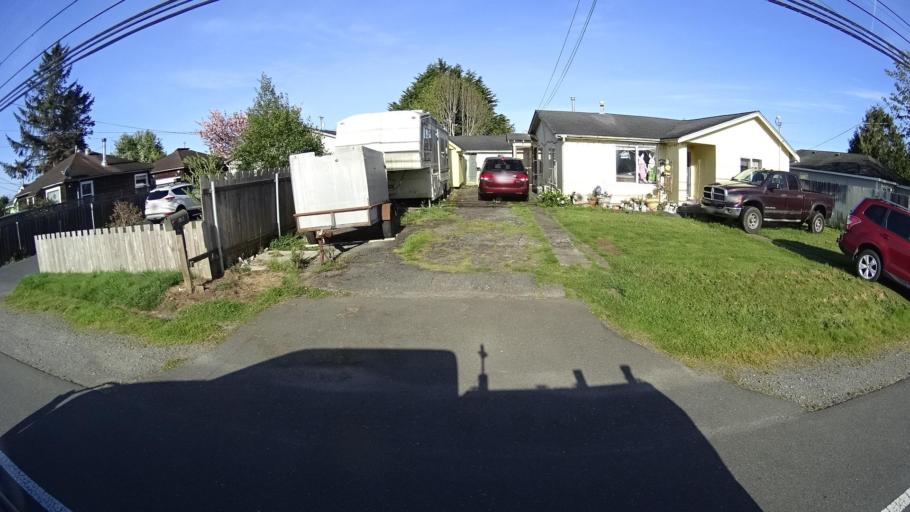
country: US
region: California
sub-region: Humboldt County
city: Bayview
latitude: 40.7648
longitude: -124.1754
